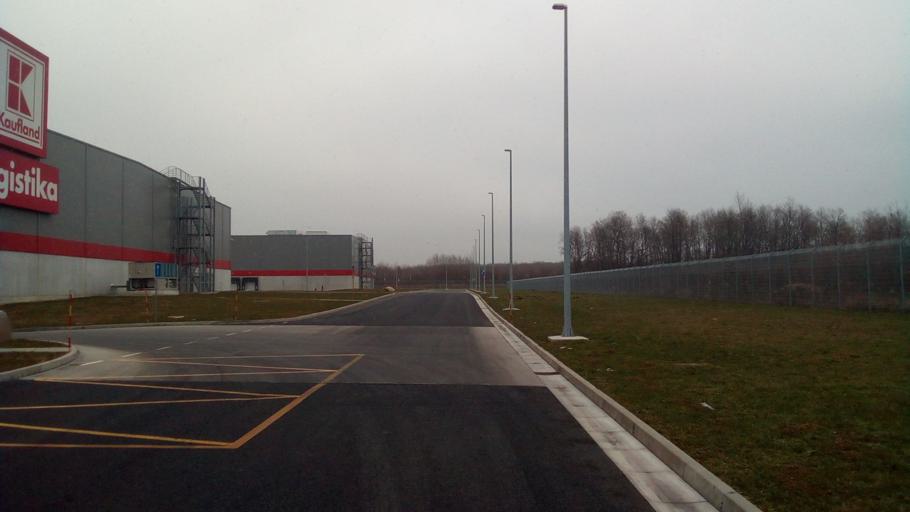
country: HR
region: Zagrebacka
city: Jastrebarsko
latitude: 45.6501
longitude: 15.6821
